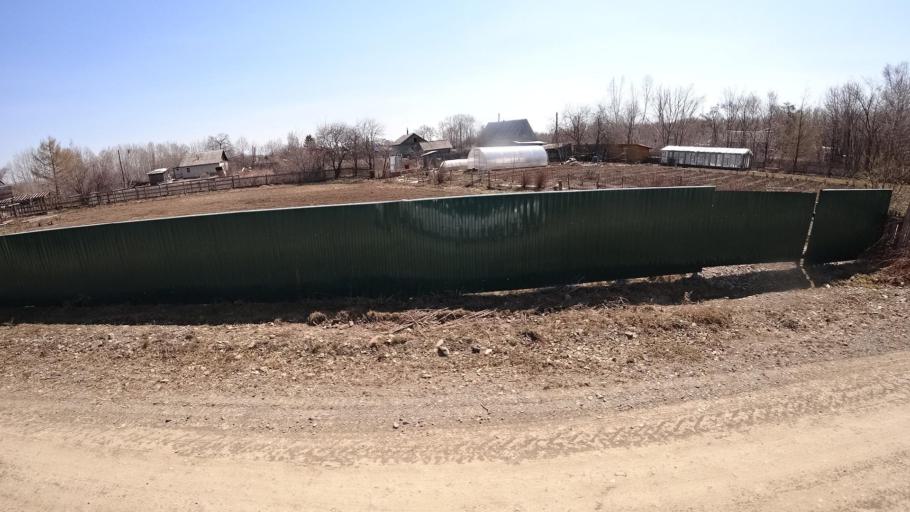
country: RU
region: Khabarovsk Krai
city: Khurba
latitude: 50.4108
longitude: 136.8615
